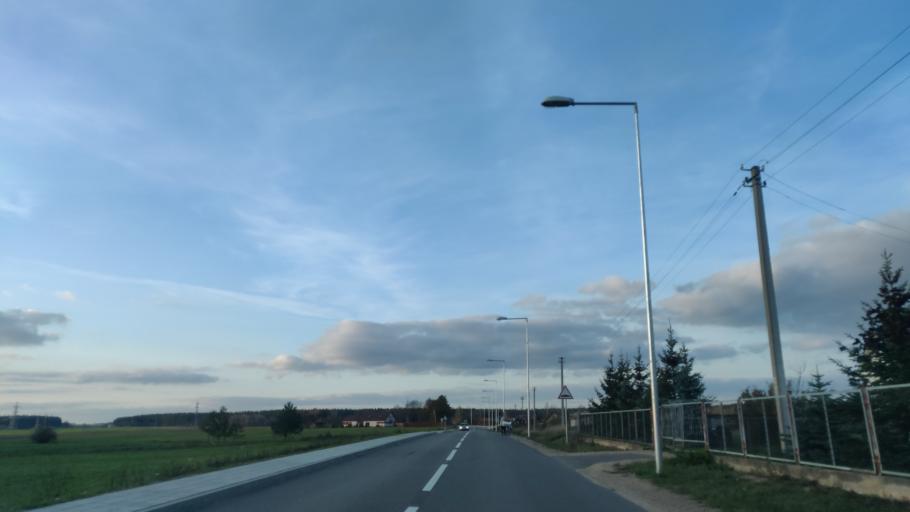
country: LT
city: Lentvaris
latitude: 54.5889
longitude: 25.0504
